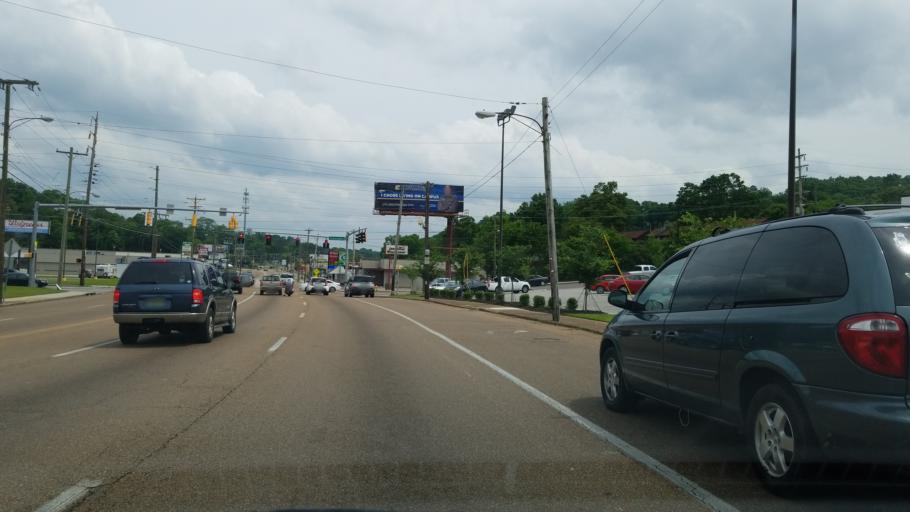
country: US
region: Tennessee
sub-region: Hamilton County
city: East Ridge
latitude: 35.0245
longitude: -85.2473
